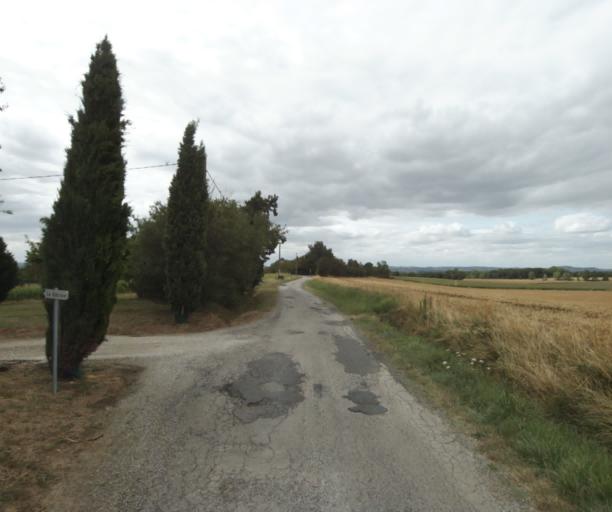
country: FR
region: Midi-Pyrenees
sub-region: Departement du Tarn
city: Soreze
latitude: 43.4603
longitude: 2.0678
